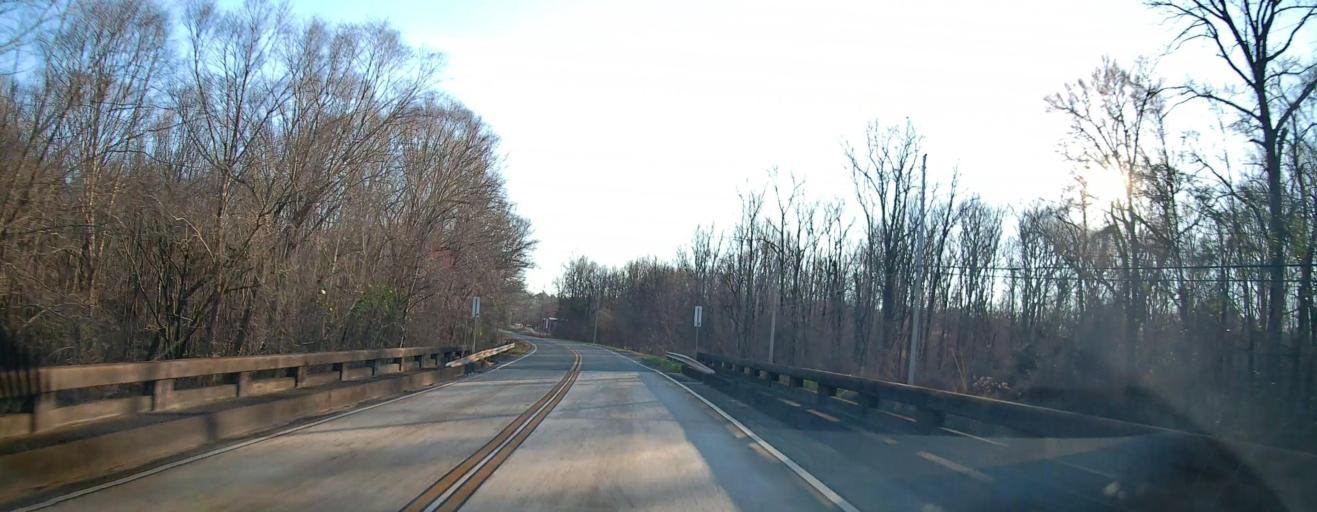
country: US
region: Georgia
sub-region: Harris County
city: Pine Mountain
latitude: 32.9136
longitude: -84.8006
